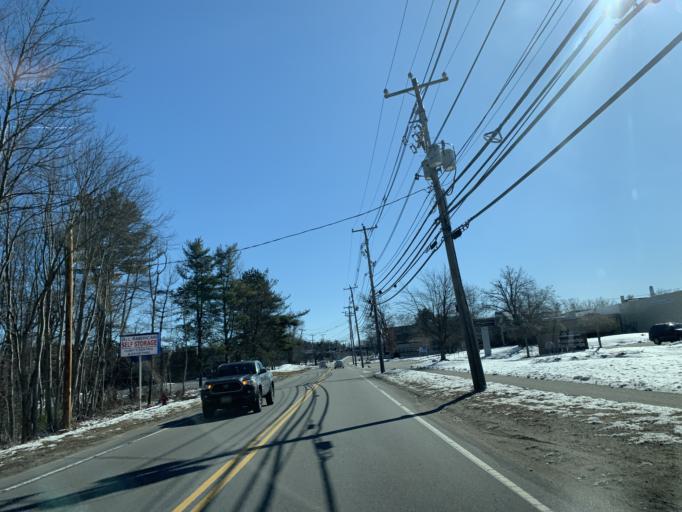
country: US
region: Massachusetts
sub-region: Middlesex County
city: Lowell
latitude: 42.5962
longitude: -71.3228
